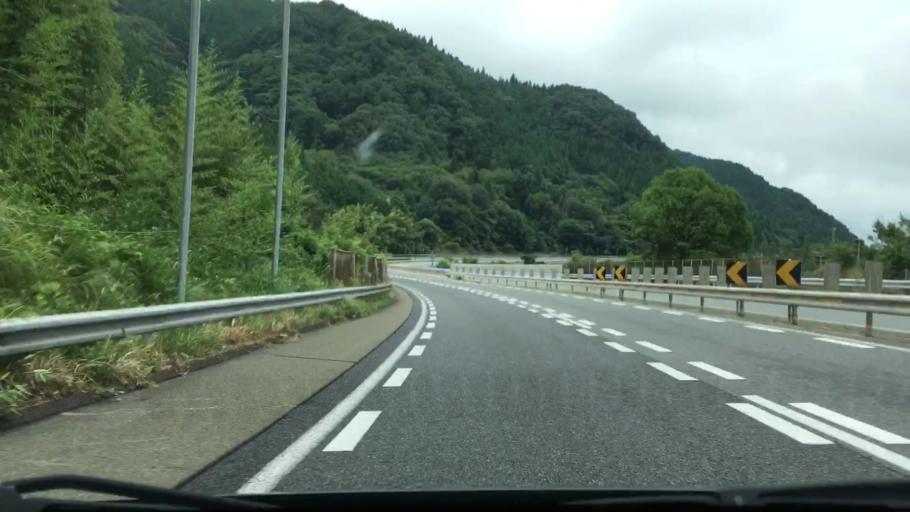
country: JP
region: Hiroshima
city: Shobara
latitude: 34.8506
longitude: 133.0928
